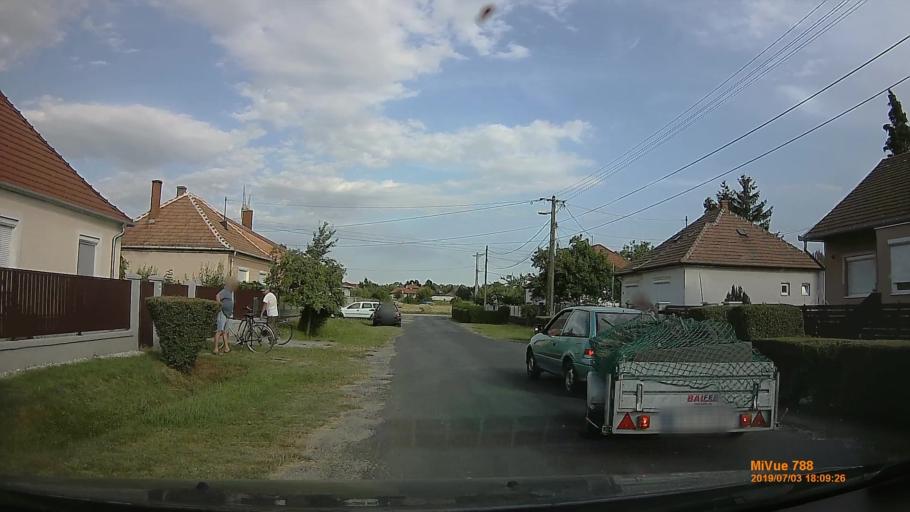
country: HU
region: Gyor-Moson-Sopron
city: Gyorujbarat
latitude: 47.6359
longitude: 17.5980
